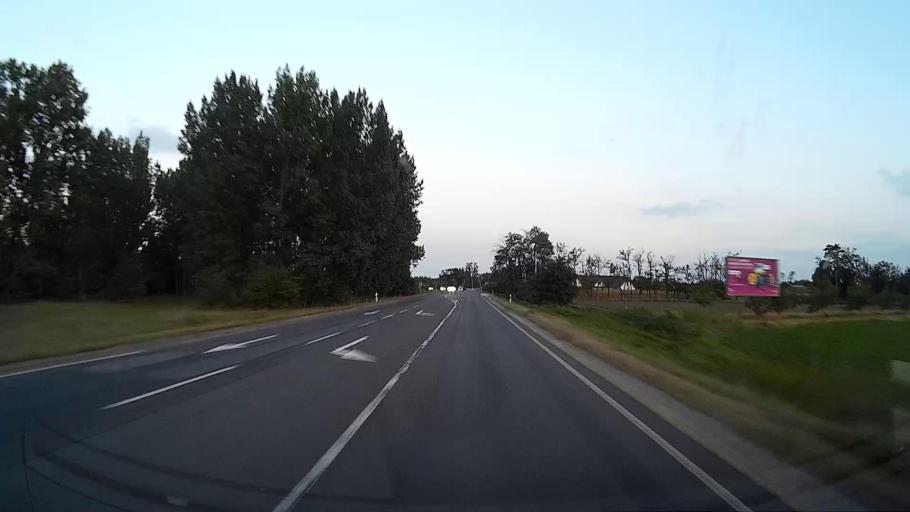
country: HU
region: Pest
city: Pilis
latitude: 47.2779
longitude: 19.5566
